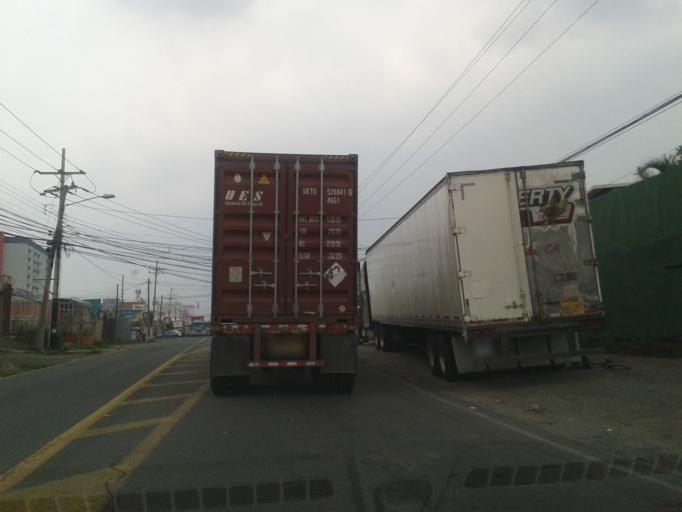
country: CR
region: Heredia
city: San Francisco
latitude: 9.9679
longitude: -84.1225
